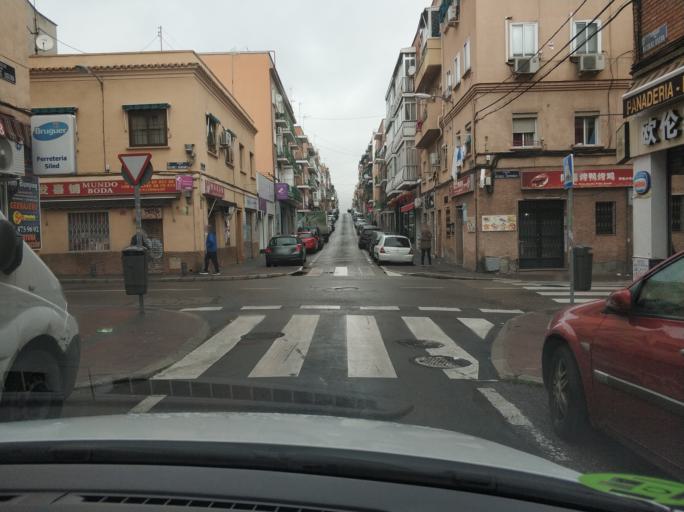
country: ES
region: Madrid
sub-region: Provincia de Madrid
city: Usera
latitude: 40.3832
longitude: -3.7053
